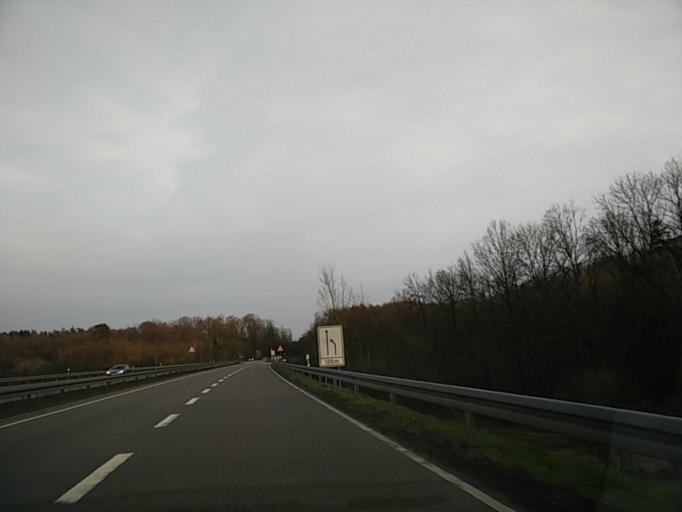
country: DE
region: Baden-Wuerttemberg
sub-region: Regierungsbezirk Stuttgart
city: Boeblingen
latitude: 48.6733
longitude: 8.9805
